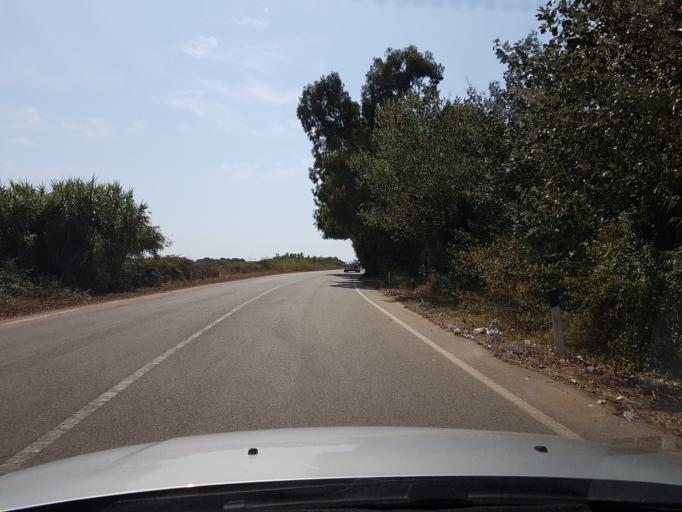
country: IT
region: Sardinia
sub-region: Provincia di Oristano
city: Solanas
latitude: 39.9201
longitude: 8.5443
